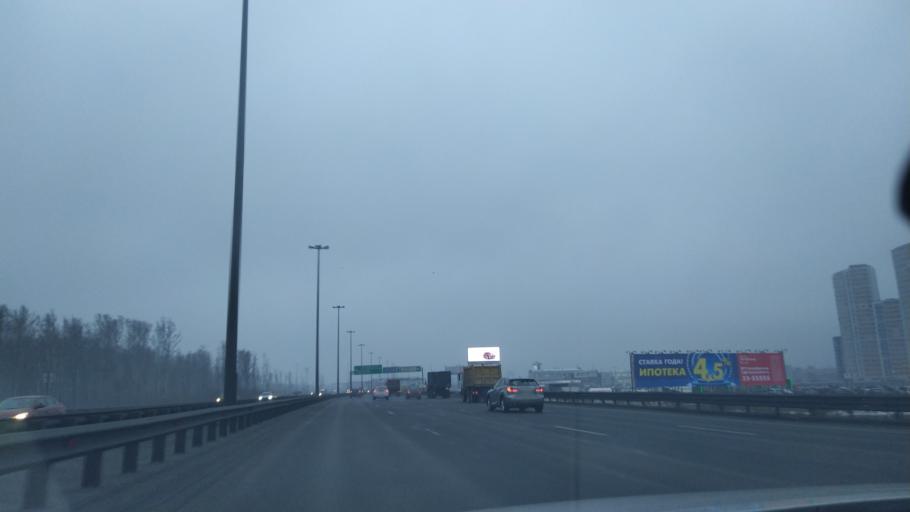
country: RU
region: Leningrad
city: Rybatskoye
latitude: 59.9022
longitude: 30.5263
